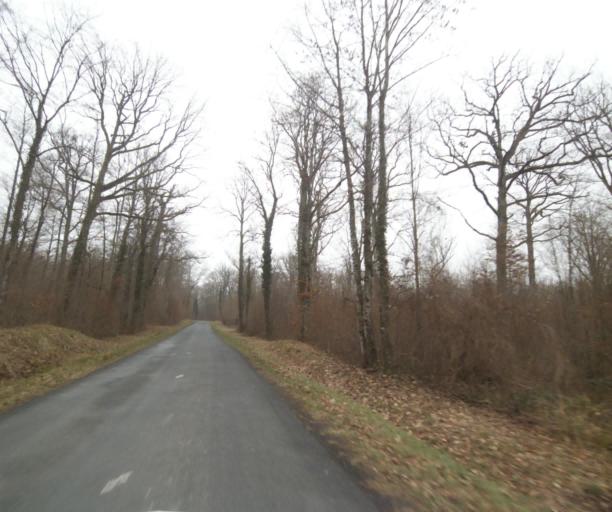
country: FR
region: Champagne-Ardenne
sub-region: Departement de la Haute-Marne
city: Bienville
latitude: 48.5647
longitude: 5.0145
